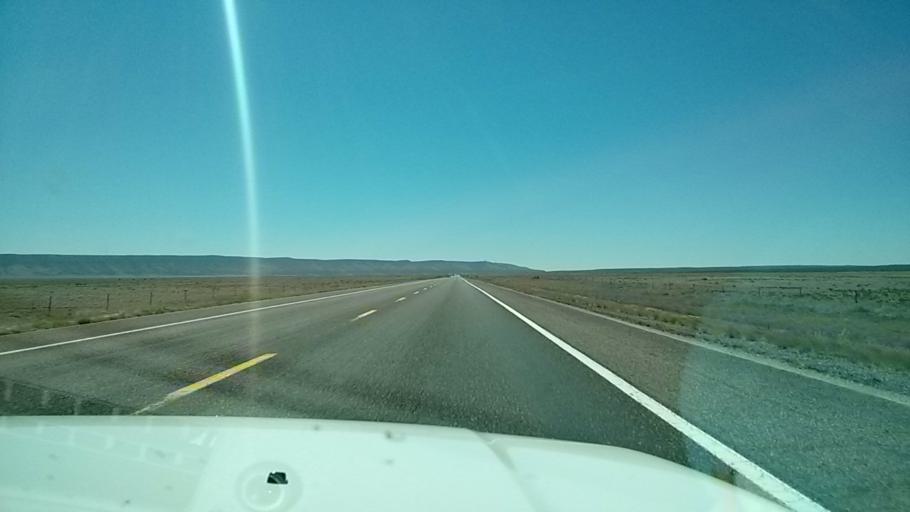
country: US
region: Arizona
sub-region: Mohave County
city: Peach Springs
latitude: 35.4352
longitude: -113.0700
